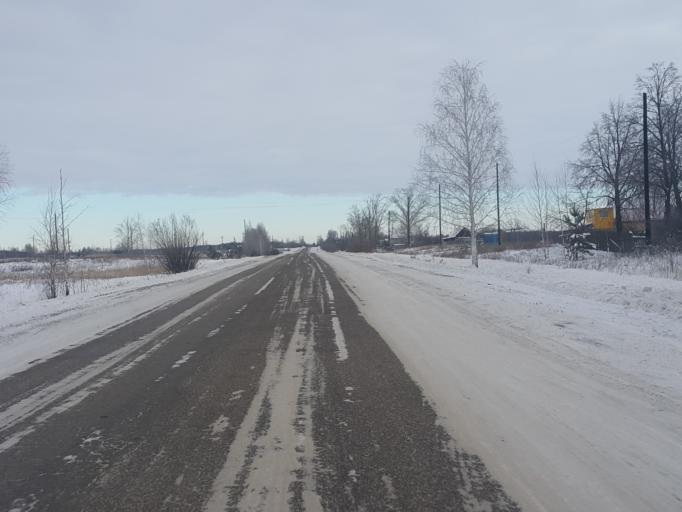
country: RU
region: Tambov
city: Platonovka
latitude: 52.8571
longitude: 41.8320
